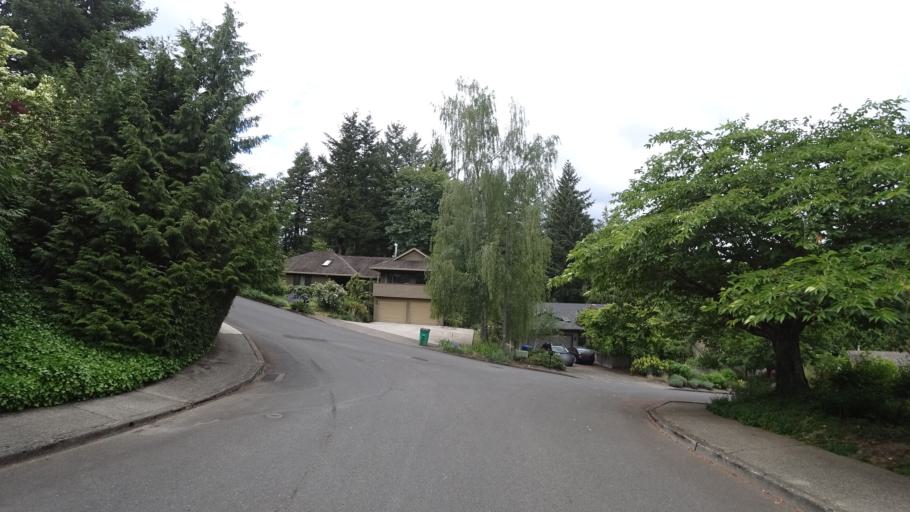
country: US
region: Oregon
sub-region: Clackamas County
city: Lake Oswego
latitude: 45.4533
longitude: -122.6991
